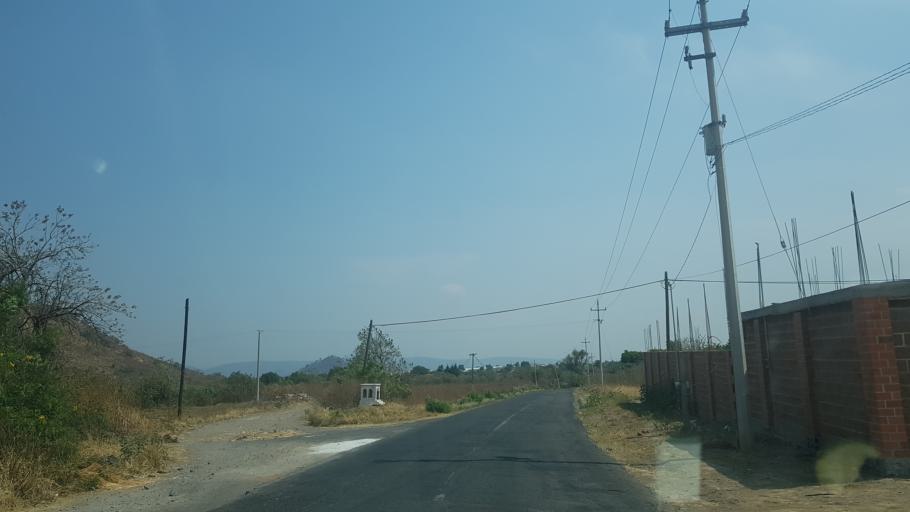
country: MX
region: Puebla
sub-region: Tianguismanalco
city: San Martin Tlapala
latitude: 18.9468
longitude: -98.4540
